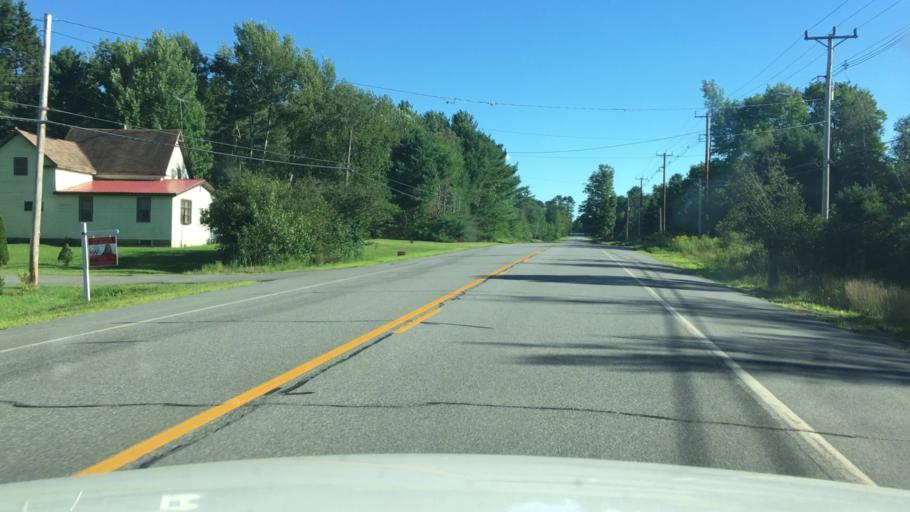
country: US
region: Maine
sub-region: Penobscot County
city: Howland
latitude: 45.1807
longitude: -68.6181
